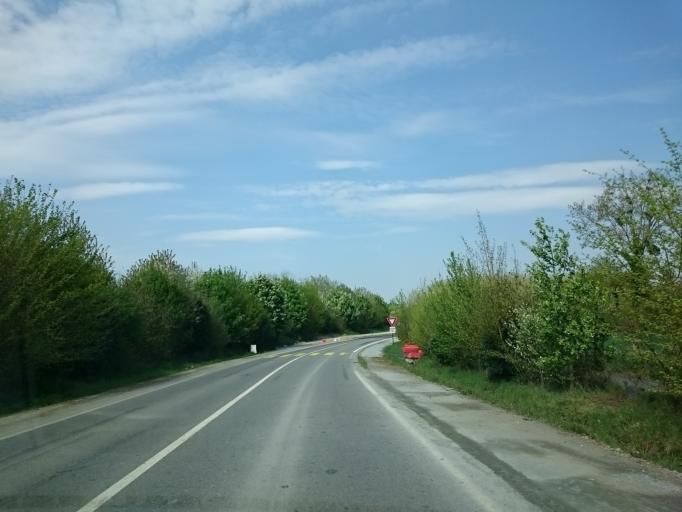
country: FR
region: Brittany
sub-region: Departement d'Ille-et-Vilaine
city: Vern-sur-Seiche
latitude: 48.0340
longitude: -1.6000
